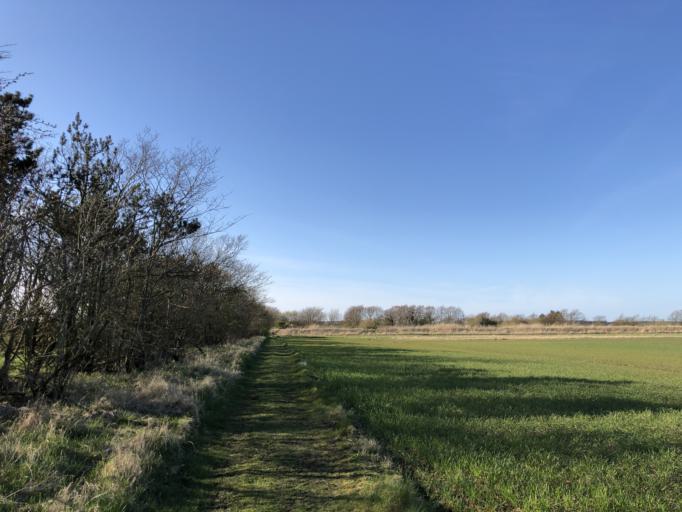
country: DK
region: Central Jutland
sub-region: Holstebro Kommune
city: Ulfborg
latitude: 56.3297
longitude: 8.3143
